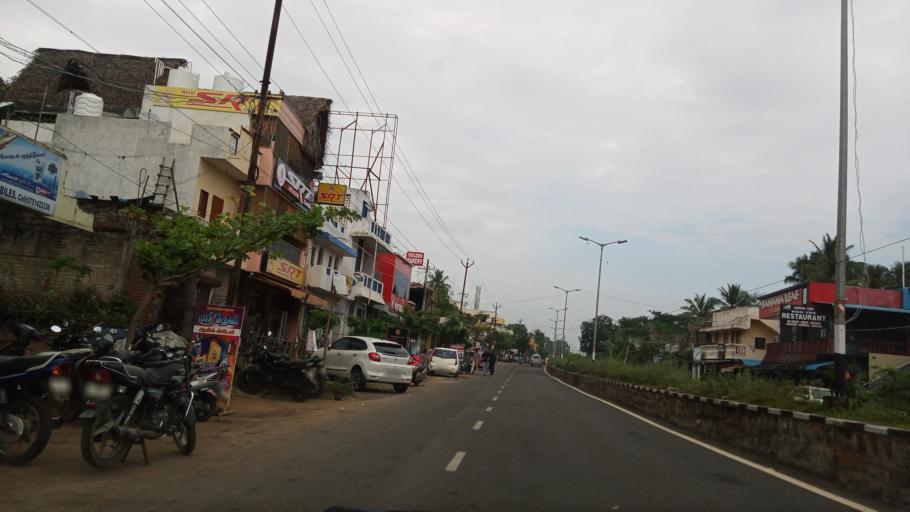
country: IN
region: Tamil Nadu
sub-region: Villupuram
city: Auroville
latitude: 12.0211
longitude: 79.8602
